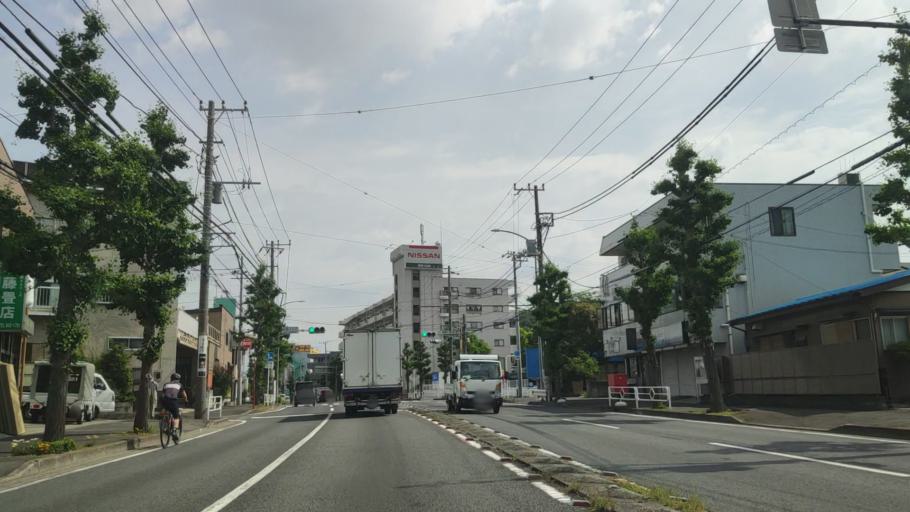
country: JP
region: Kanagawa
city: Kamakura
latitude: 35.3872
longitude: 139.5814
